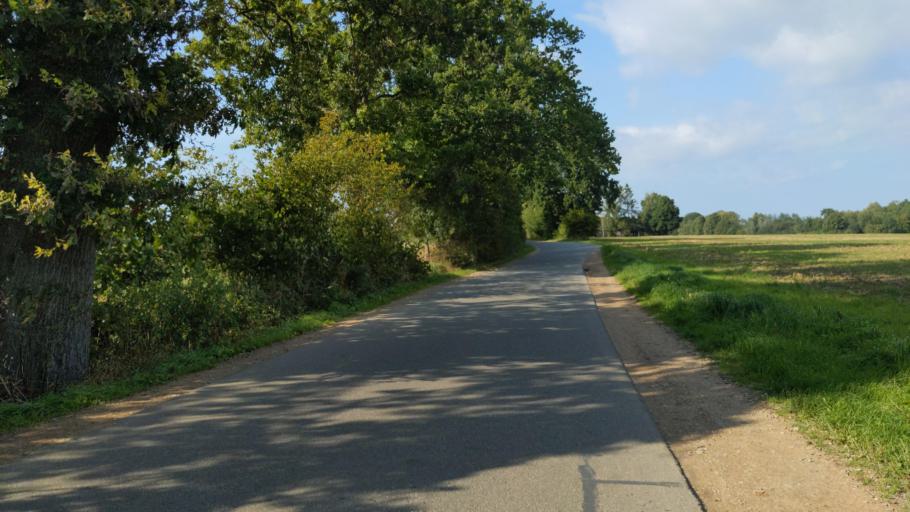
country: DE
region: Mecklenburg-Vorpommern
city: Kalkhorst
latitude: 53.9734
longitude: 11.0101
